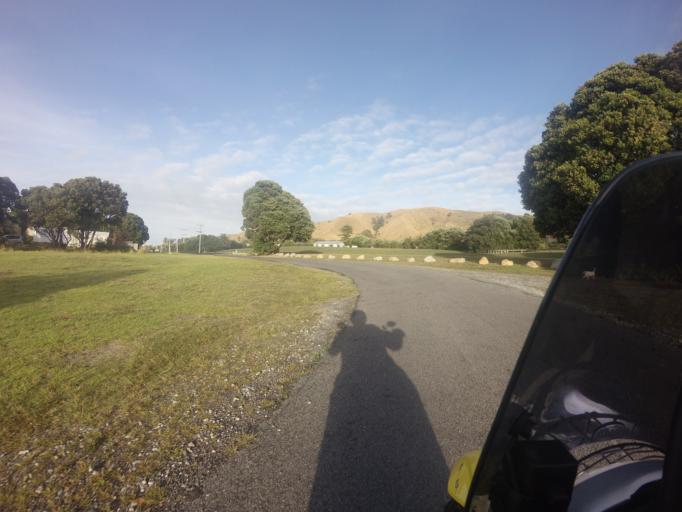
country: NZ
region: Gisborne
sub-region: Gisborne District
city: Gisborne
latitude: -38.6785
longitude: 178.0797
